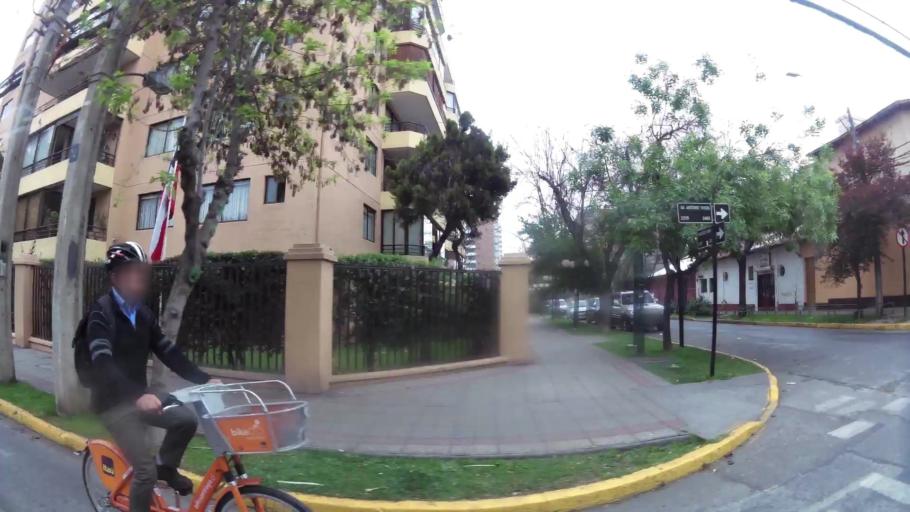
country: CL
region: Santiago Metropolitan
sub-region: Provincia de Santiago
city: Villa Presidente Frei, Nunoa, Santiago, Chile
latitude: -33.4496
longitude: -70.6104
